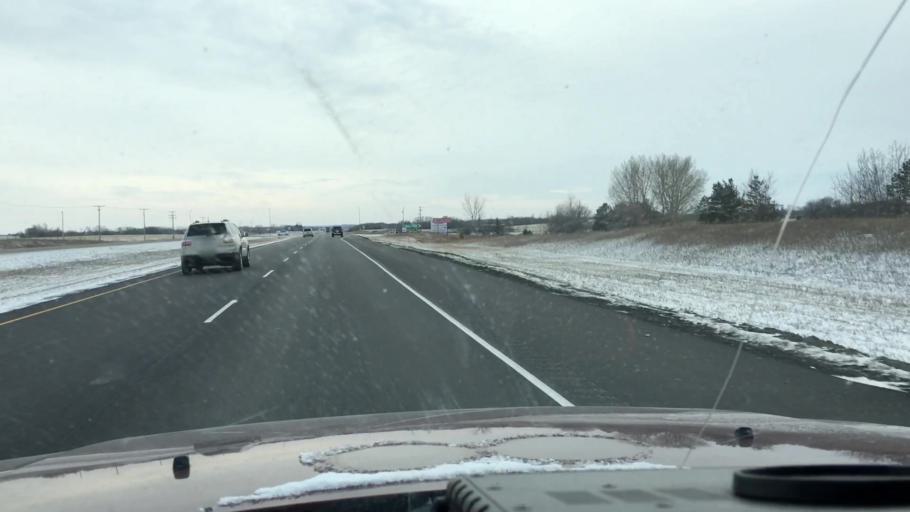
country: CA
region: Saskatchewan
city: Saskatoon
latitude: 52.0300
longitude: -106.5838
